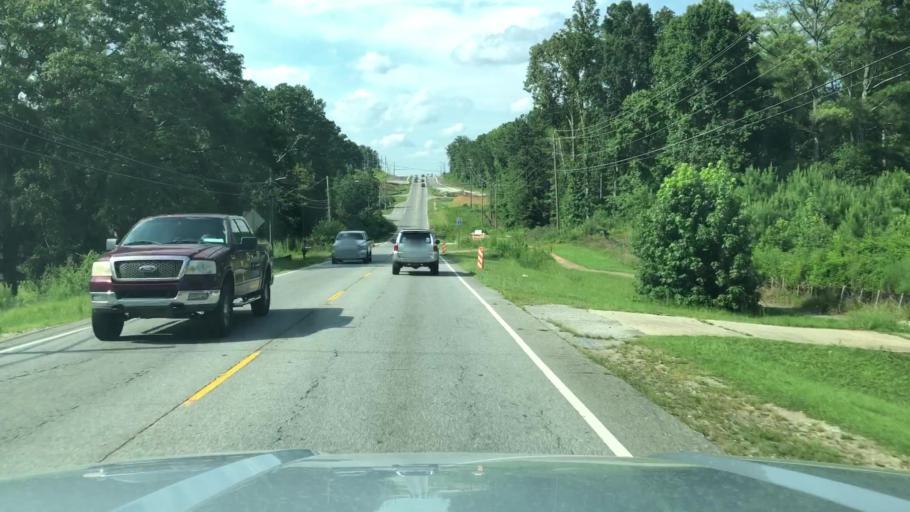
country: US
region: Georgia
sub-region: Douglas County
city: Douglasville
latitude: 33.7619
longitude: -84.7489
